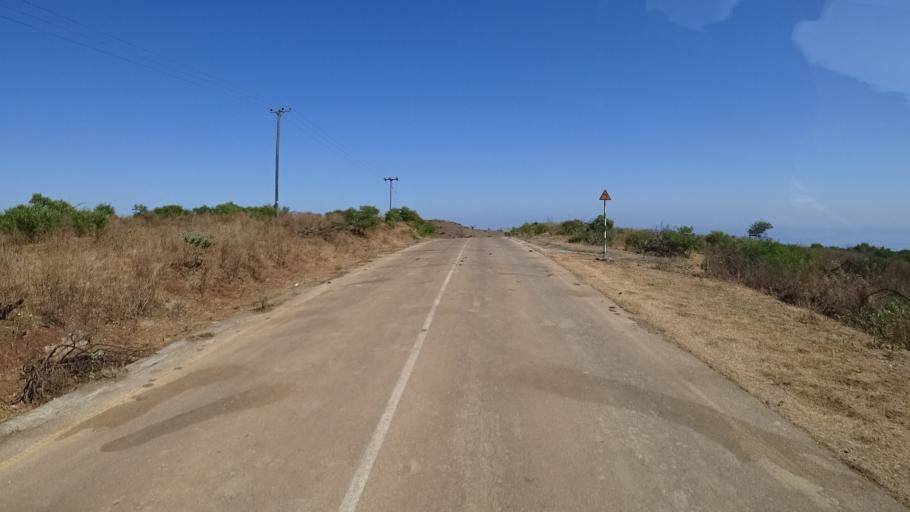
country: YE
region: Al Mahrah
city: Hawf
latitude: 16.7450
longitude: 53.3495
